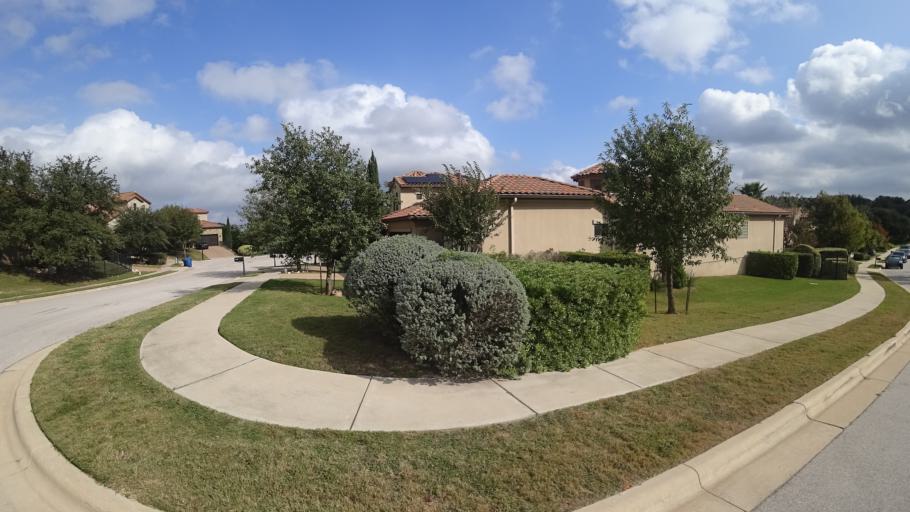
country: US
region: Texas
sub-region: Travis County
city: Bee Cave
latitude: 30.3111
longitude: -97.9061
